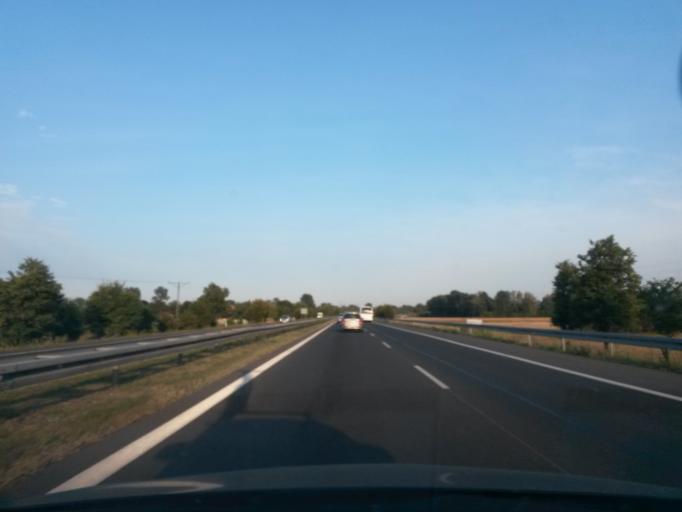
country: PL
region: Masovian Voivodeship
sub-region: Powiat nowodworski
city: Nowy Dwor Mazowiecki
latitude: 52.4160
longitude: 20.6826
